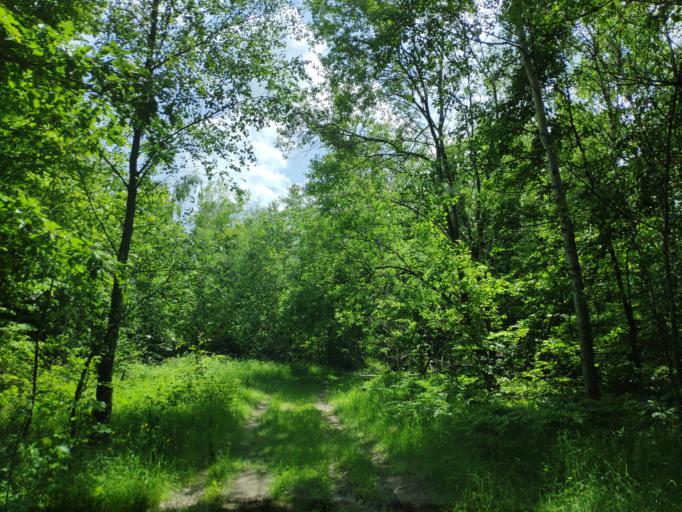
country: SK
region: Kosicky
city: Medzev
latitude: 48.7223
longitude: 20.9545
